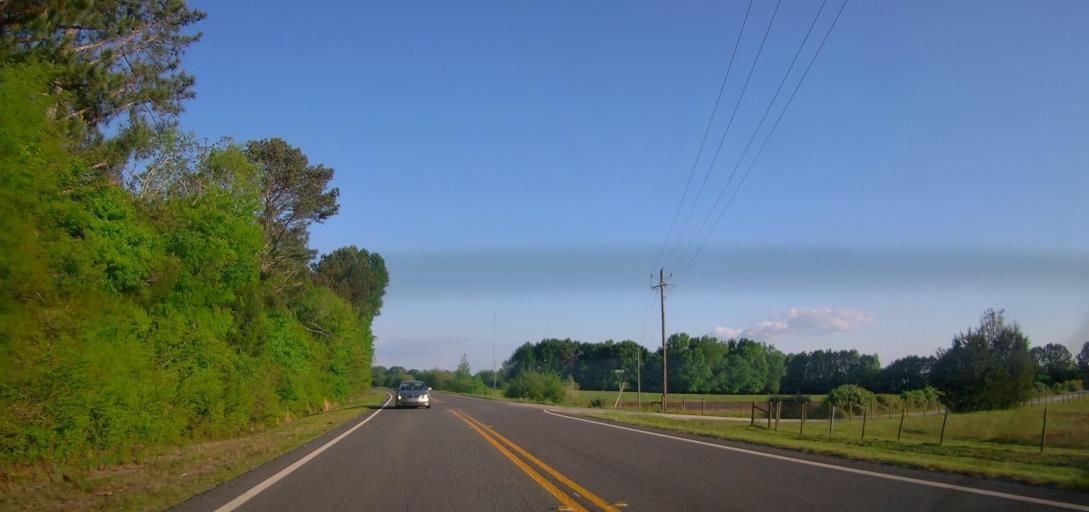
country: US
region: Georgia
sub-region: Jasper County
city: Monticello
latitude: 33.4504
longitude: -83.6289
